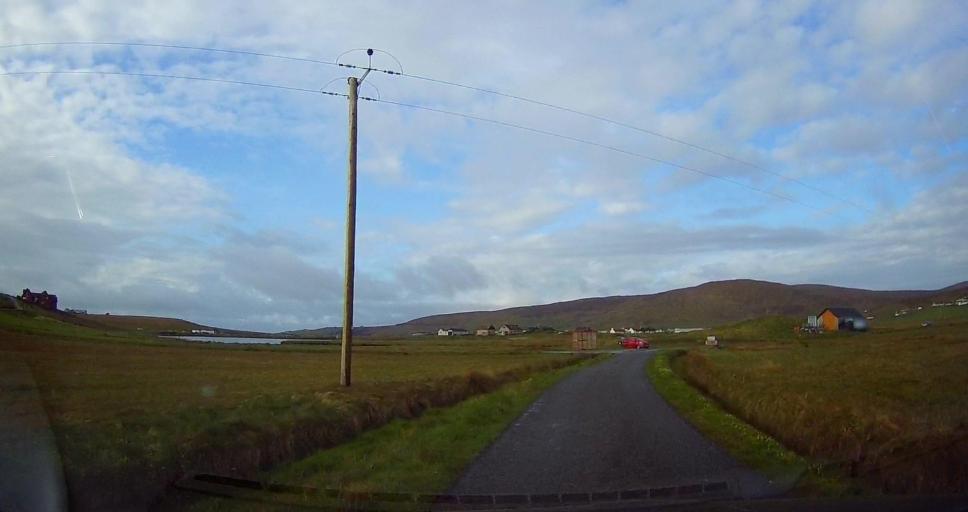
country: GB
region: Scotland
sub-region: Shetland Islands
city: Sandwick
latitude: 60.0473
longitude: -1.2078
